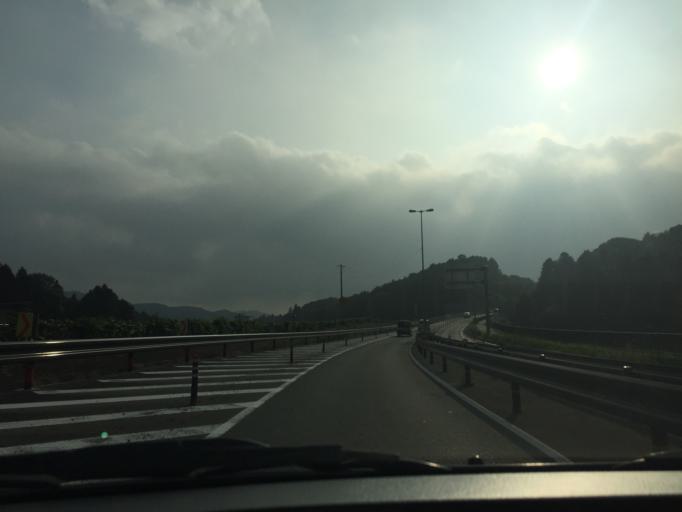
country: JP
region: Aichi
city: Shinshiro
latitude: 34.9168
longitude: 137.5335
